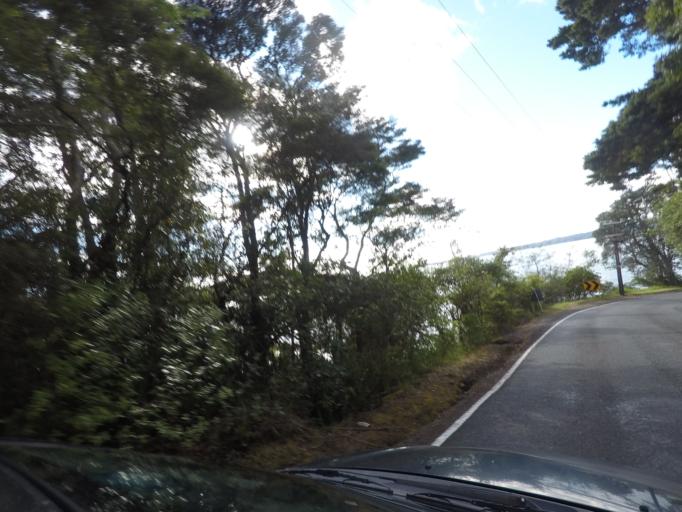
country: NZ
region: Auckland
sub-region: Auckland
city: Titirangi
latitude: -37.0086
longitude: 174.5627
